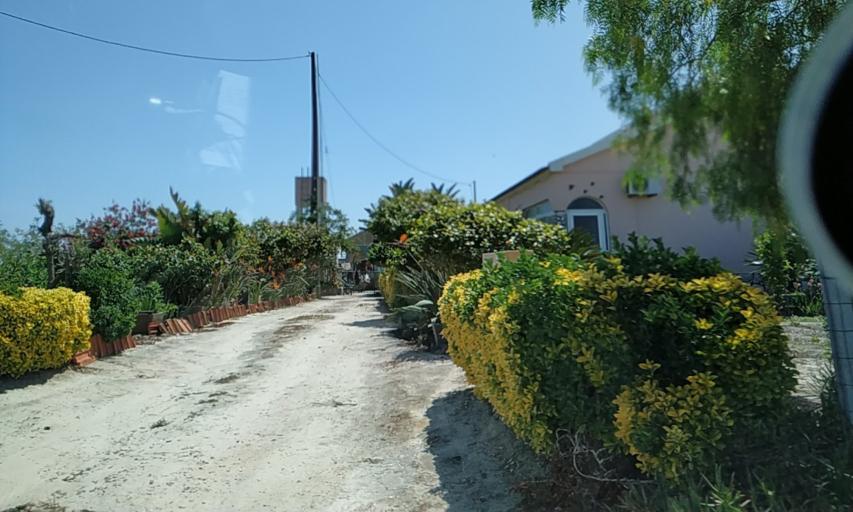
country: PT
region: Setubal
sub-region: Palmela
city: Palmela
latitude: 38.6027
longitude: -8.8129
